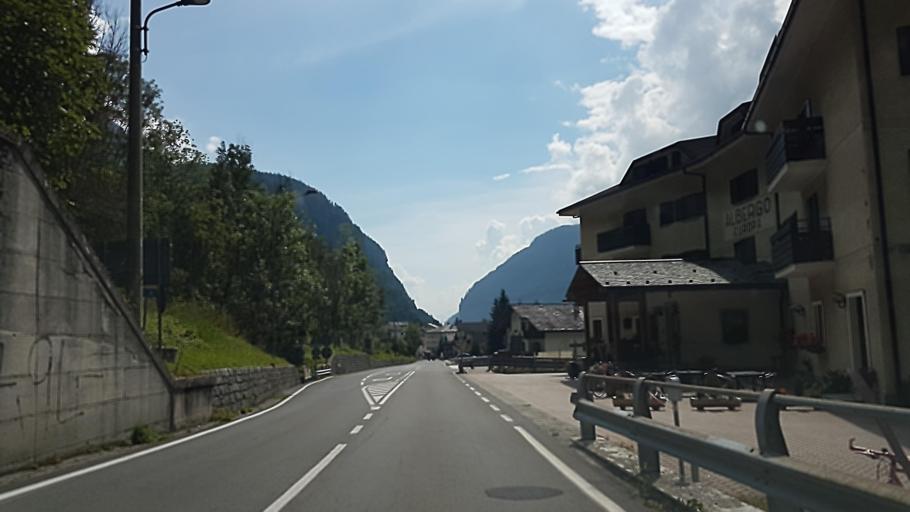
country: IT
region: Lombardy
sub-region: Provincia di Sondrio
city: Campodolcino
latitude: 46.4097
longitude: 9.3508
